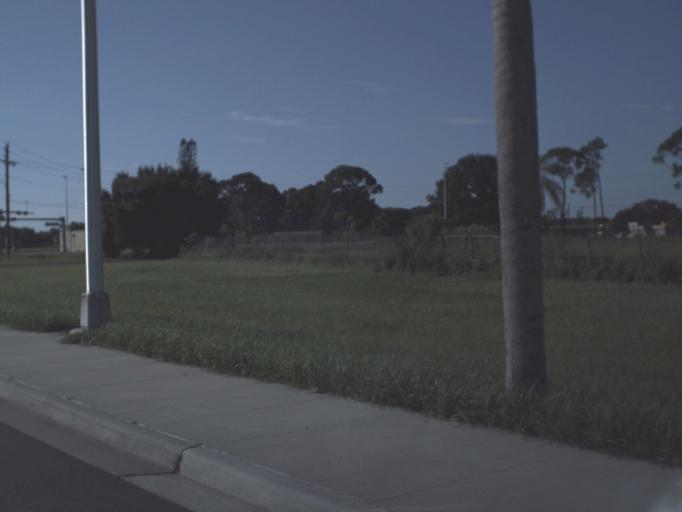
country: US
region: Florida
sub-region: Lee County
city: Fort Myers
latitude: 26.6191
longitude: -81.8604
